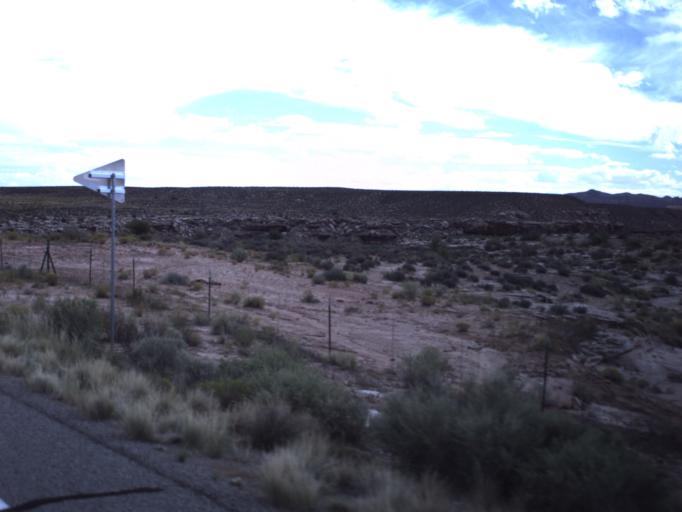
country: US
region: Utah
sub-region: San Juan County
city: Blanding
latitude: 37.2932
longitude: -109.4216
